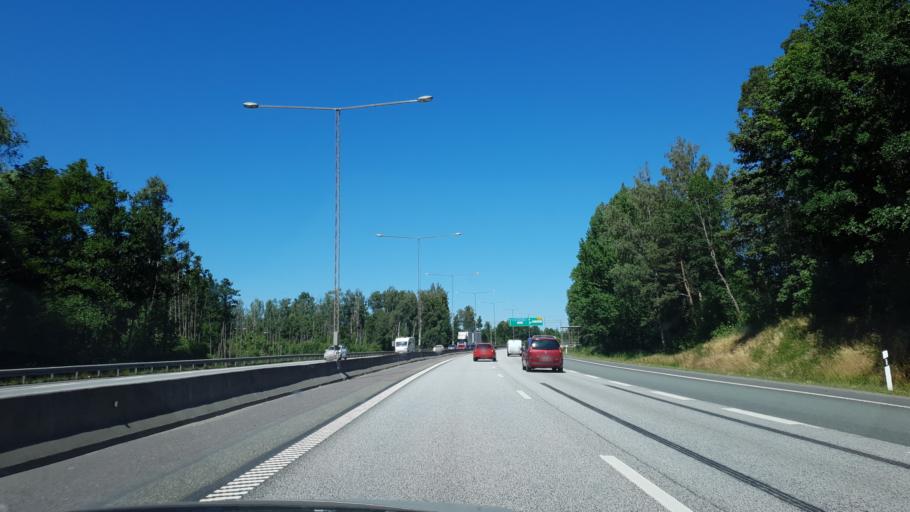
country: SE
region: Joenkoeping
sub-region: Jonkopings Kommun
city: Jonkoping
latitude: 57.7670
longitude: 14.1892
